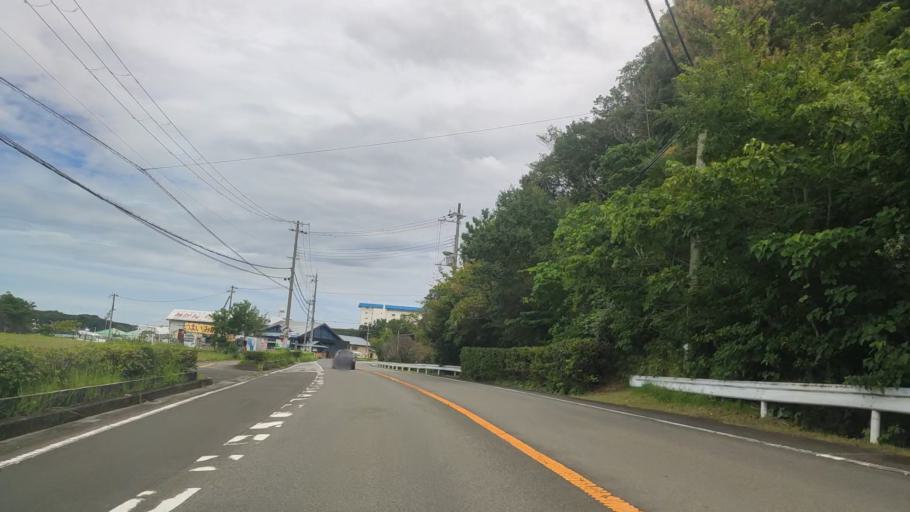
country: JP
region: Wakayama
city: Tanabe
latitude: 33.6955
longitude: 135.3885
